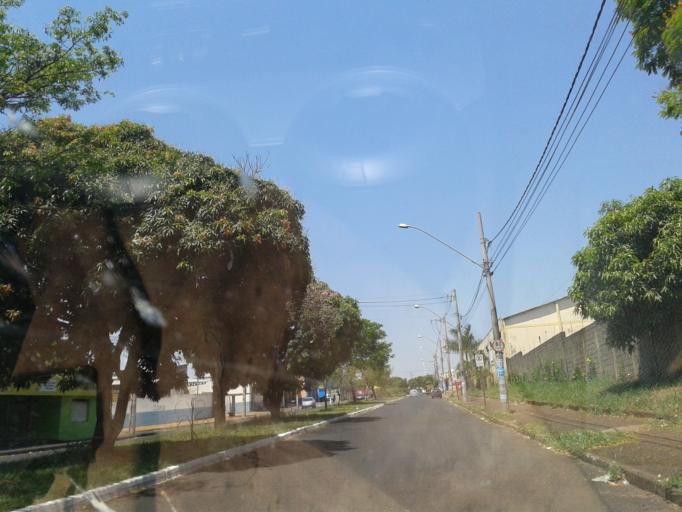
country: BR
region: Minas Gerais
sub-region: Uberlandia
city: Uberlandia
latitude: -18.9362
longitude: -48.3055
